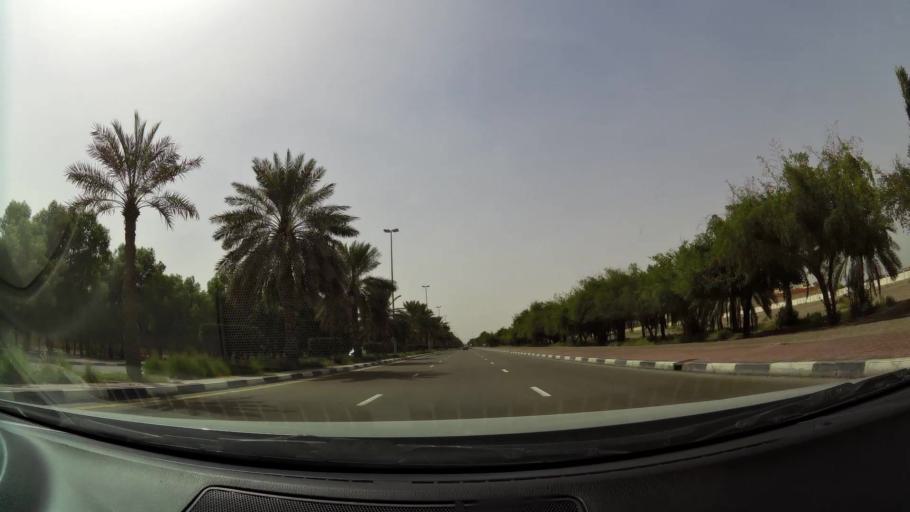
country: AE
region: Abu Dhabi
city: Al Ain
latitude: 24.1790
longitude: 55.6625
